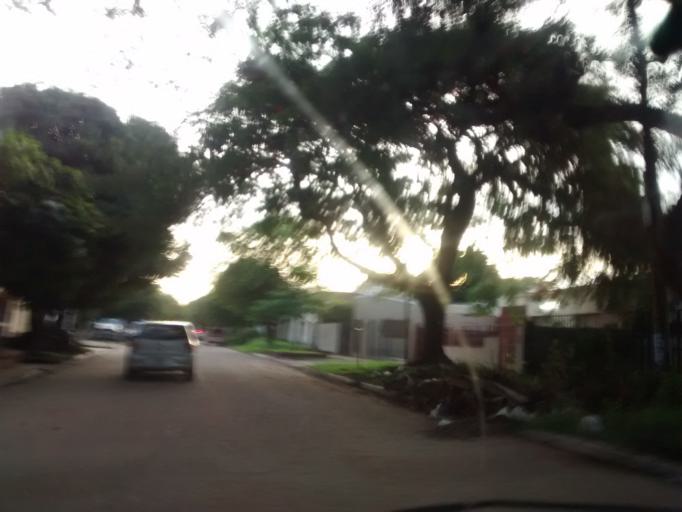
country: AR
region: Chaco
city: Resistencia
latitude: -27.4386
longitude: -58.9957
